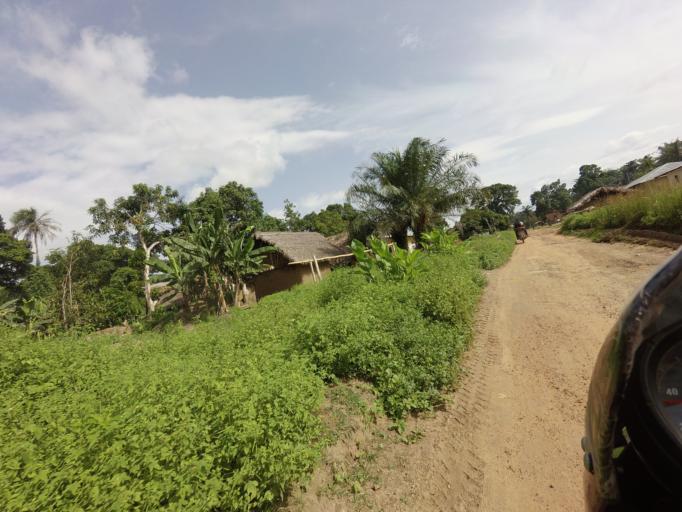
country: SL
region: Eastern Province
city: Jojoima
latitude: 7.8283
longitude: -10.8119
